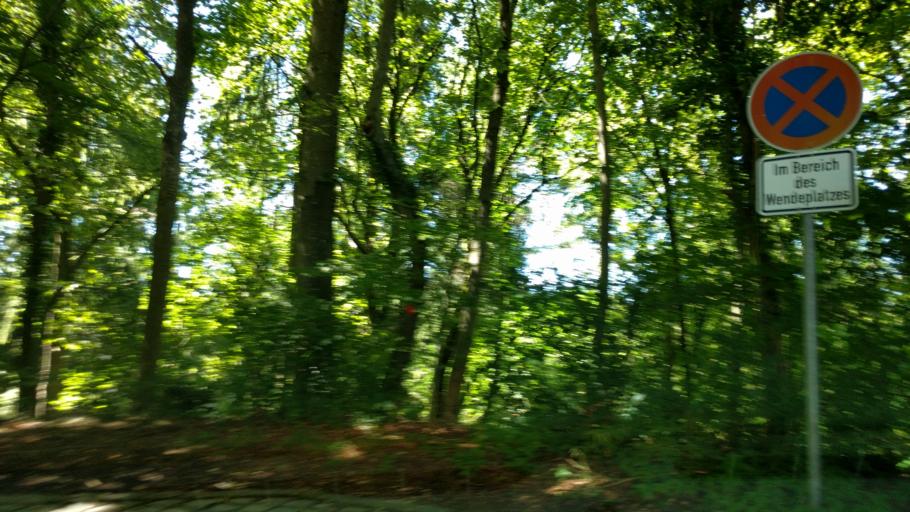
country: DE
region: Bavaria
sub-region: Upper Bavaria
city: Grunwald
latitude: 48.0467
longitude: 11.5233
